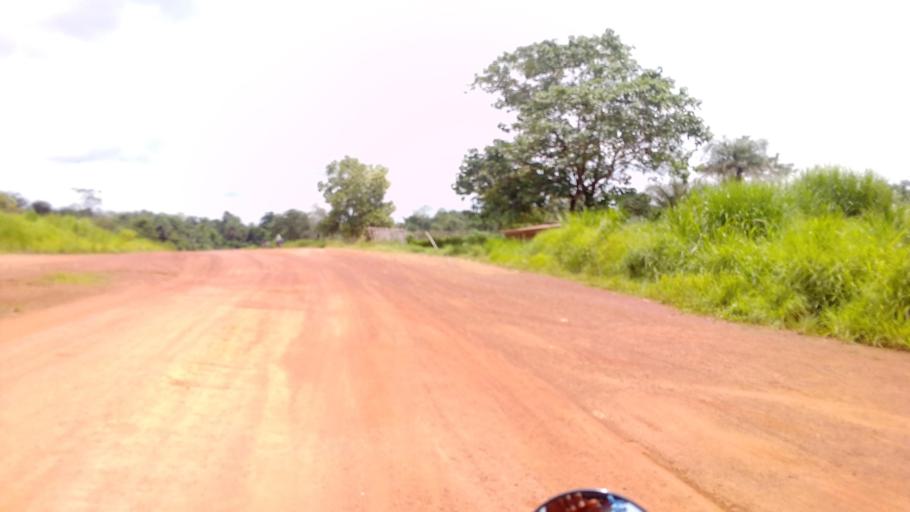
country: SL
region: Northern Province
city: Makeni
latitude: 9.0730
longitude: -12.1804
